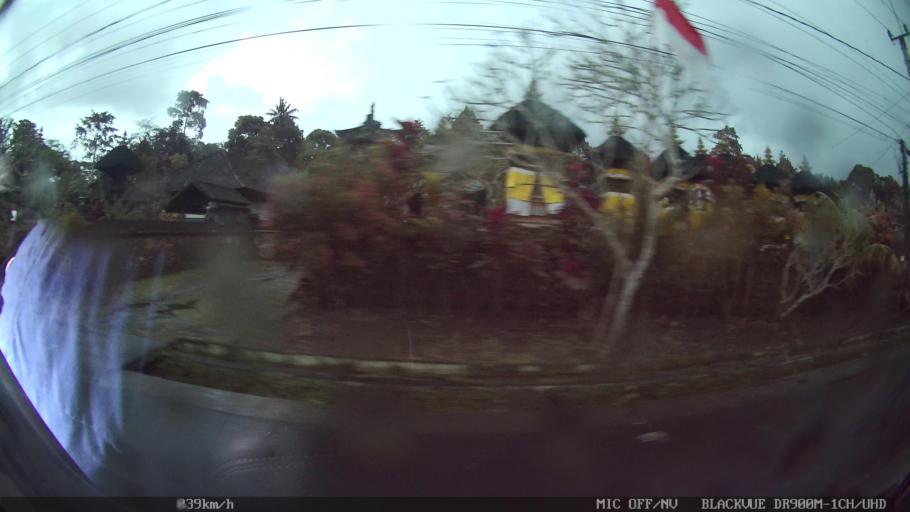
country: ID
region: Bali
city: Banjar Tengah
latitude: -8.4993
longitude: 115.1883
